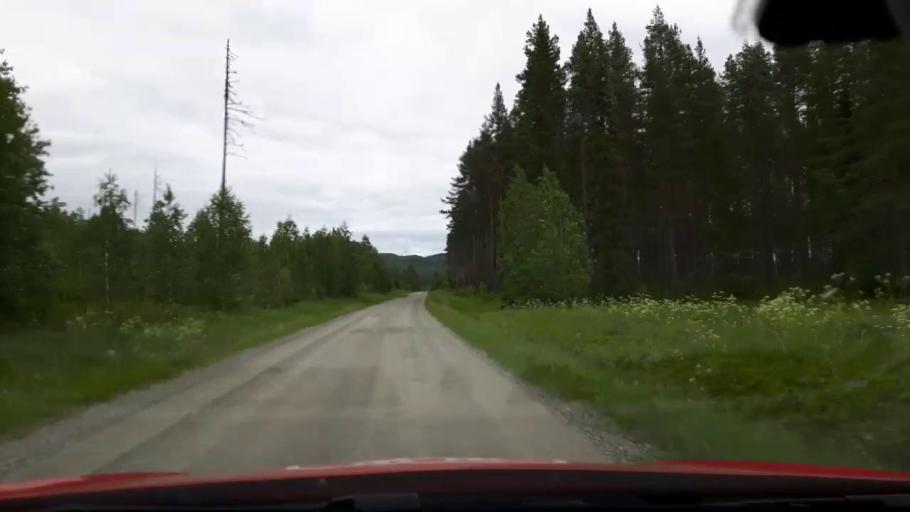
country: SE
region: Jaemtland
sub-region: Ragunda Kommun
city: Hammarstrand
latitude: 63.2139
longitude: 16.0725
